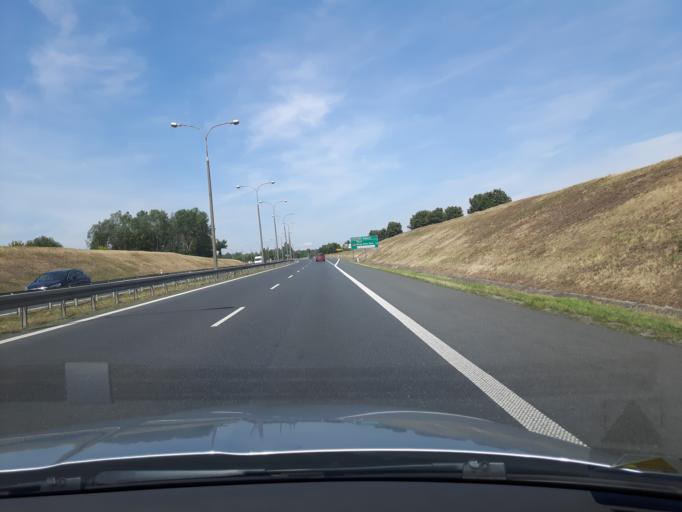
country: PL
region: Masovian Voivodeship
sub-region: Powiat nowodworski
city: Zakroczym
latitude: 52.4361
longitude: 20.6486
